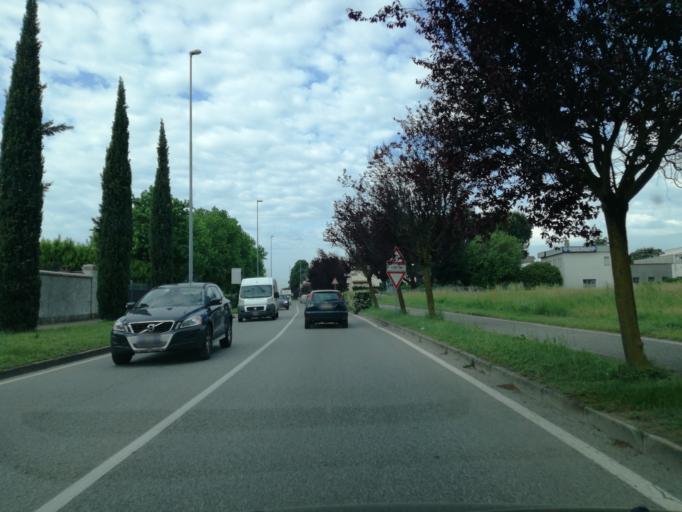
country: IT
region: Lombardy
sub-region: Provincia di Monza e Brianza
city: Albiate
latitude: 45.6561
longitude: 9.2495
